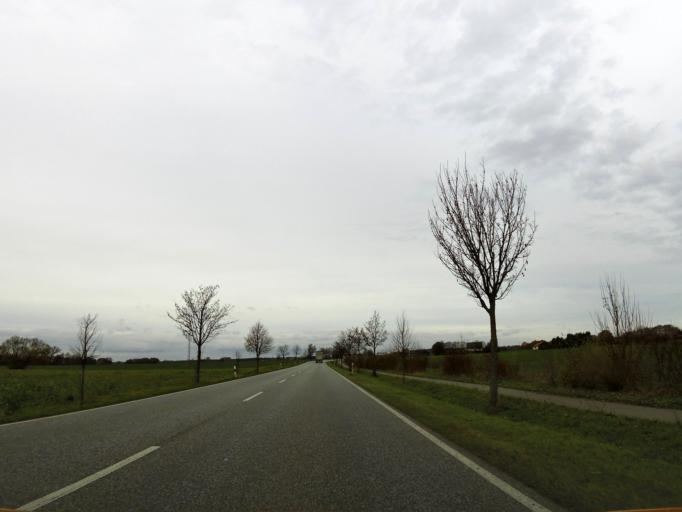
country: DE
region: Saxony-Anhalt
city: Pretzier
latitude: 52.8076
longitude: 11.2230
